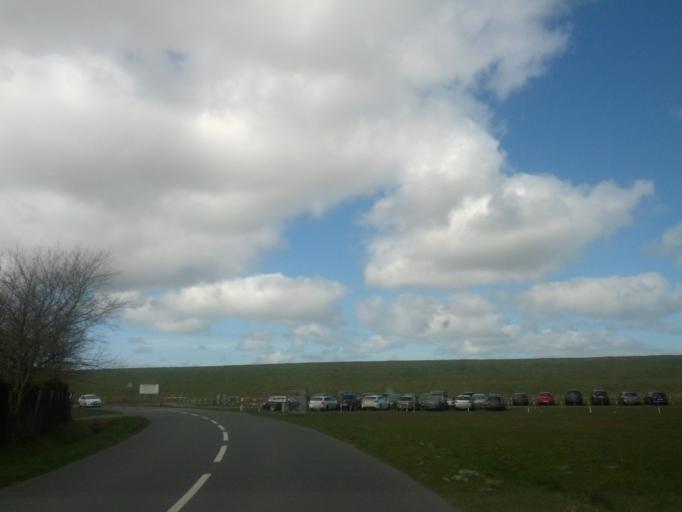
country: DE
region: Lower Saxony
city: Esens
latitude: 53.6776
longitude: 7.5844
